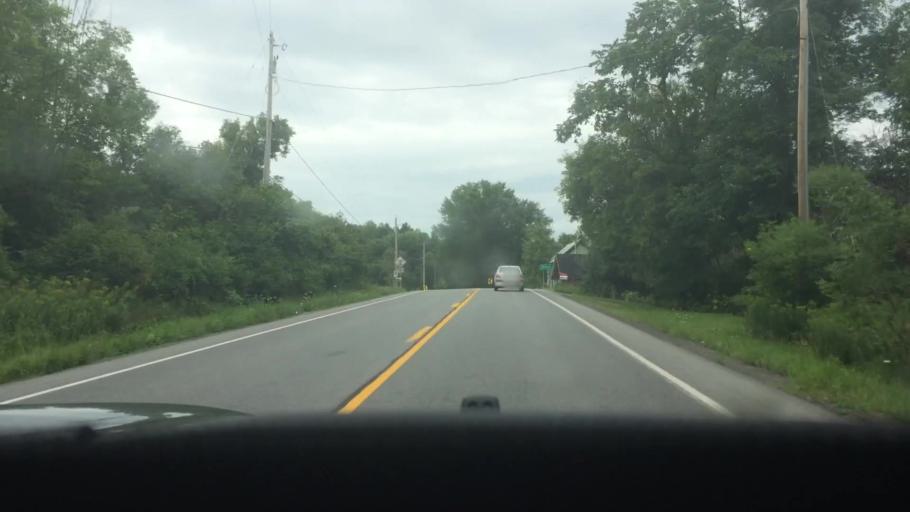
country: US
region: New York
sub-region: St. Lawrence County
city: Canton
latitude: 44.5024
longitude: -75.3425
